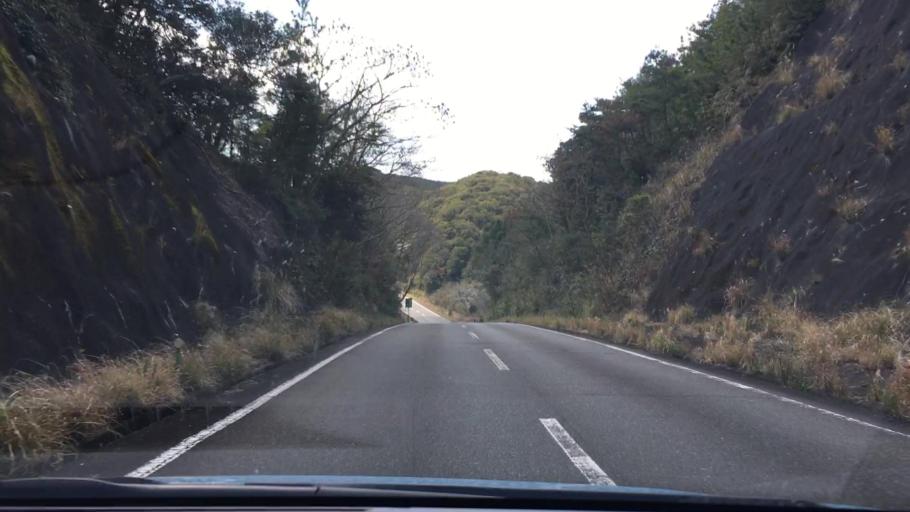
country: JP
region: Mie
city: Toba
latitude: 34.4413
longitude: 136.9109
